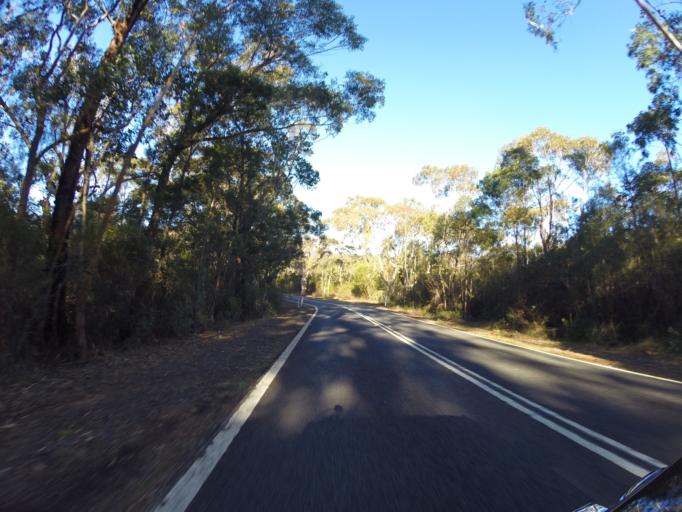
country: AU
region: New South Wales
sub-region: Wollongong
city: Helensburgh
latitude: -34.1500
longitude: 151.0127
